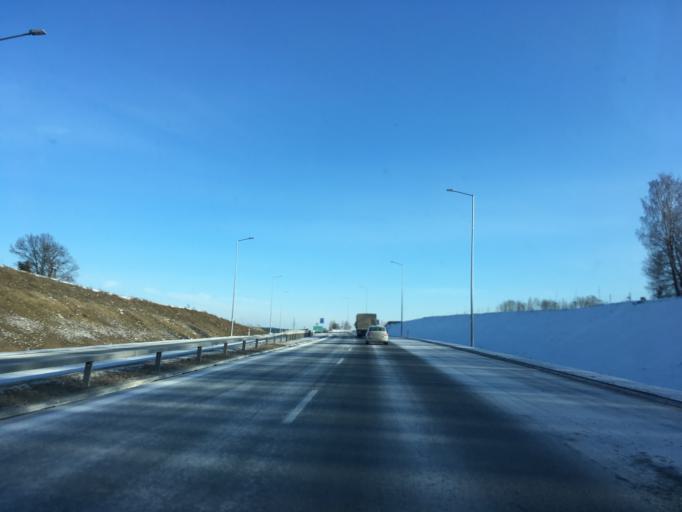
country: PL
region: Pomeranian Voivodeship
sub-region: Powiat koscierski
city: Koscierzyna
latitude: 54.1093
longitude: 17.9586
